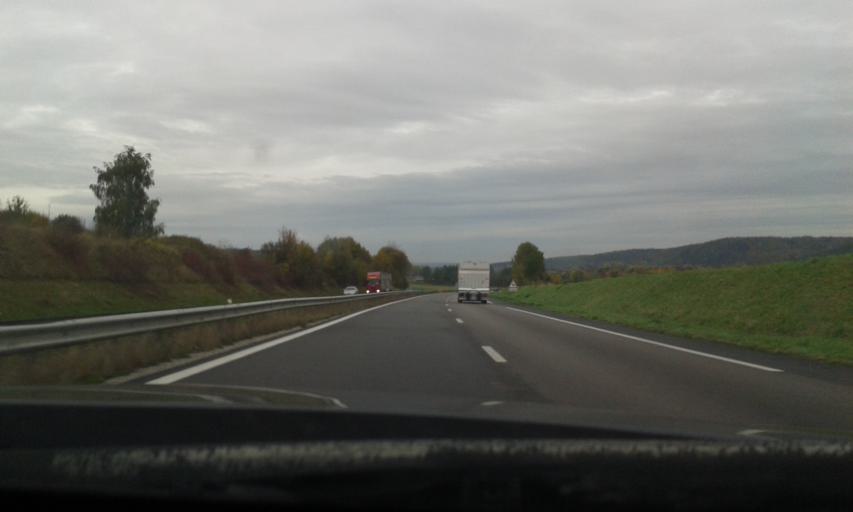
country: FR
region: Haute-Normandie
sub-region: Departement de l'Eure
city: Heudreville-sur-Eure
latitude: 49.1422
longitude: 1.1813
